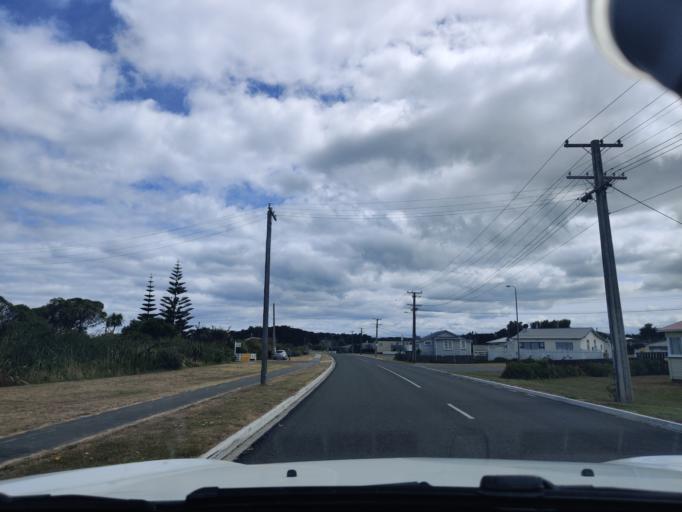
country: NZ
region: Manawatu-Wanganui
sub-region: Horowhenua District
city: Foxton
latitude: -40.4634
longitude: 175.2257
